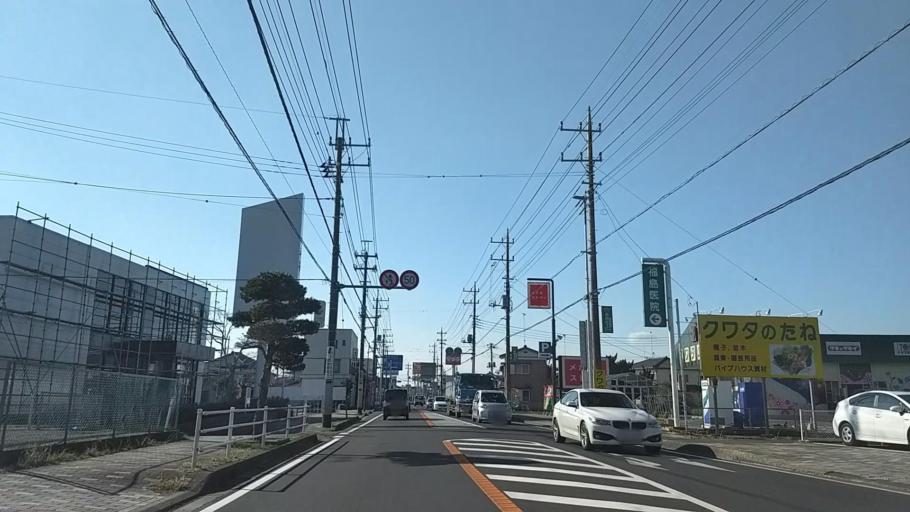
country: JP
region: Chiba
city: Yokaichiba
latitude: 35.6996
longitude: 140.5499
